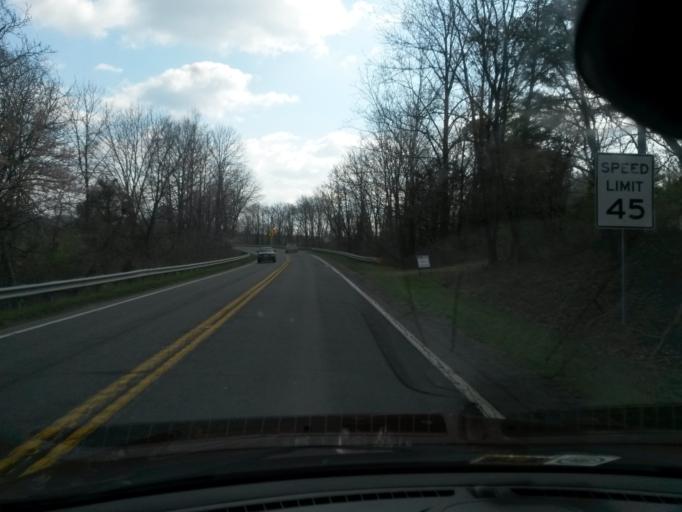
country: US
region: Virginia
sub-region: City of Waynesboro
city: Waynesboro
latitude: 38.0267
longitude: -78.8104
